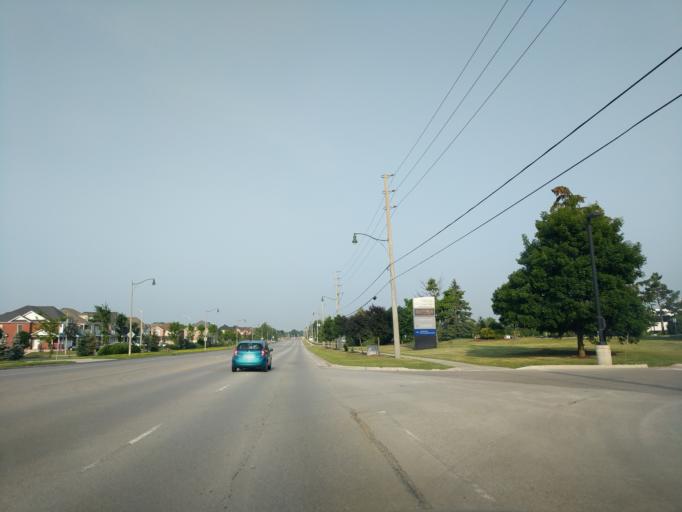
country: CA
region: Ontario
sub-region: York
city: Richmond Hill
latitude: 43.8966
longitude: -79.4042
